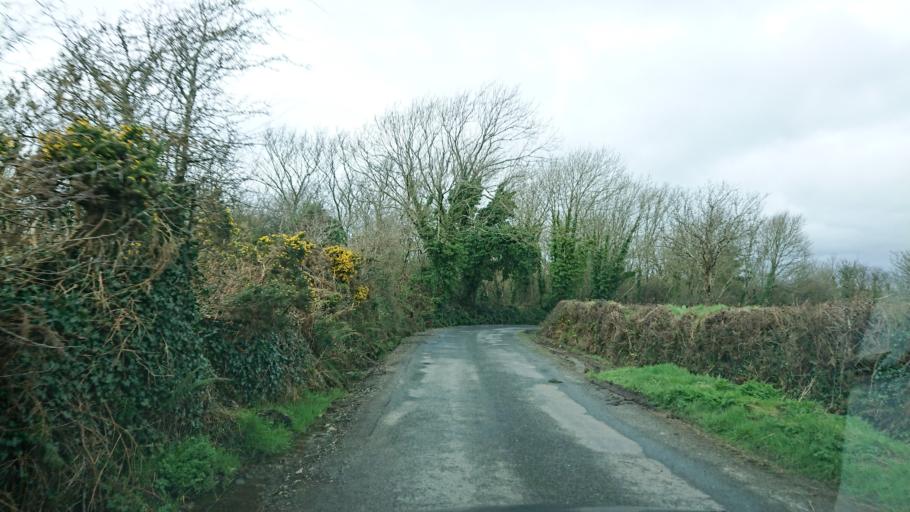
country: IE
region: Munster
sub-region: Waterford
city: Dunmore East
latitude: 52.1664
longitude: -7.0399
